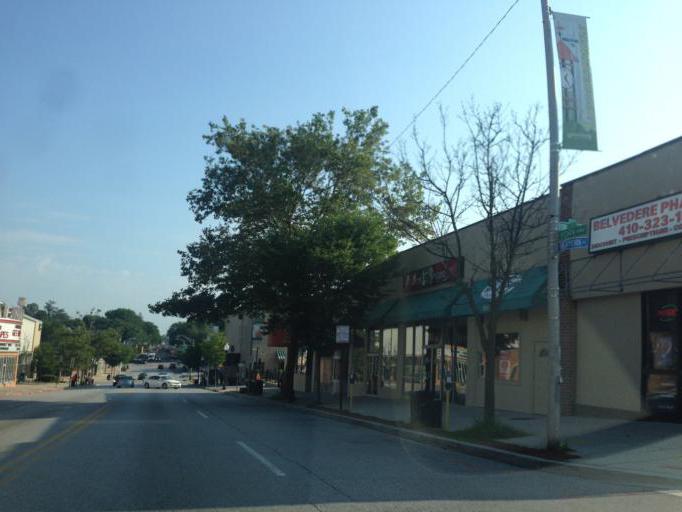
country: US
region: Maryland
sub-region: Baltimore County
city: Towson
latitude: 39.3630
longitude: -76.6100
